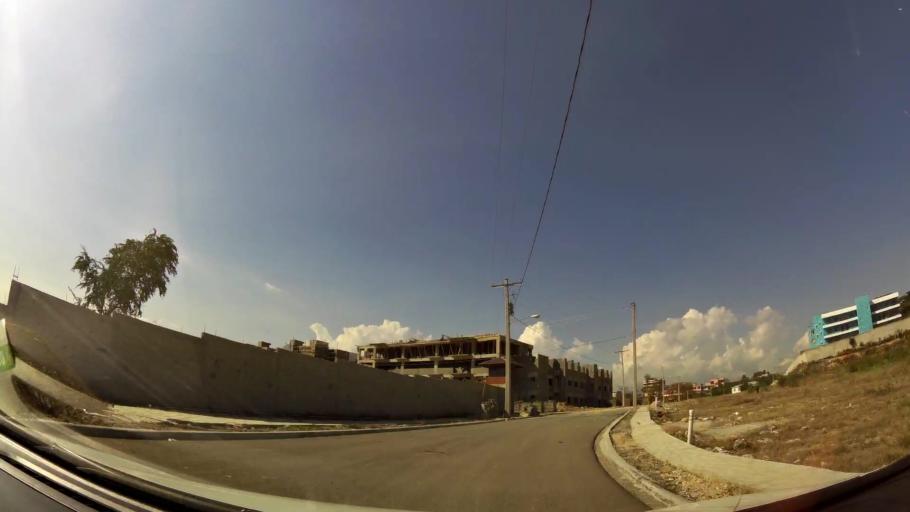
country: DO
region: Nacional
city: Bella Vista
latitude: 18.4570
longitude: -69.9812
